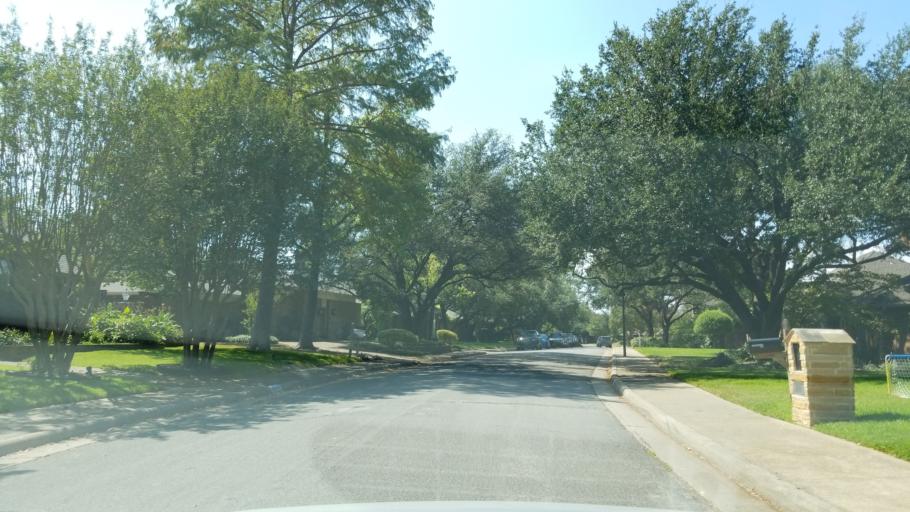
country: US
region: Texas
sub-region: Dallas County
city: Addison
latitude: 32.9701
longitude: -96.7978
